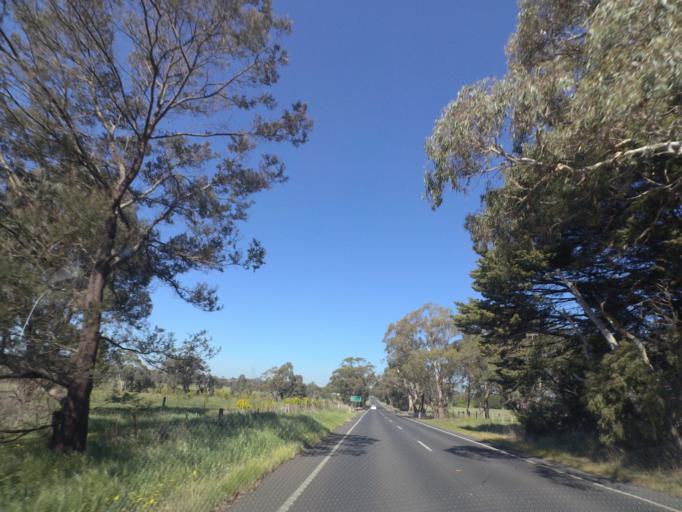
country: AU
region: Victoria
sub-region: Whittlesea
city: Whittlesea
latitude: -37.3258
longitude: 144.9637
